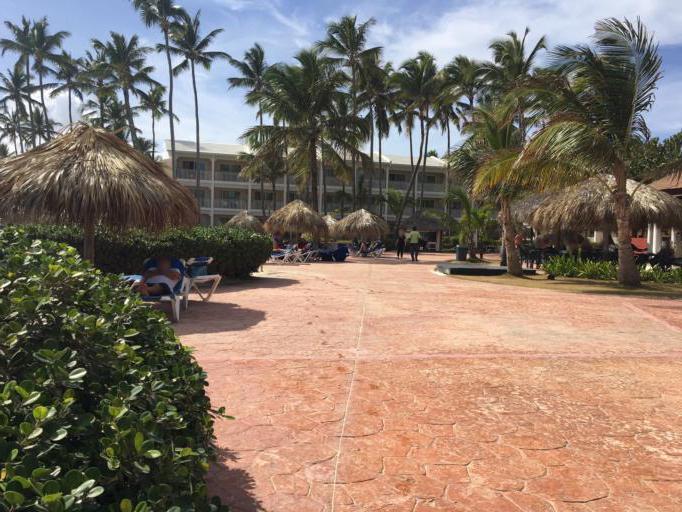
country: DO
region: San Juan
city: Punta Cana
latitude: 18.7096
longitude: -68.4421
